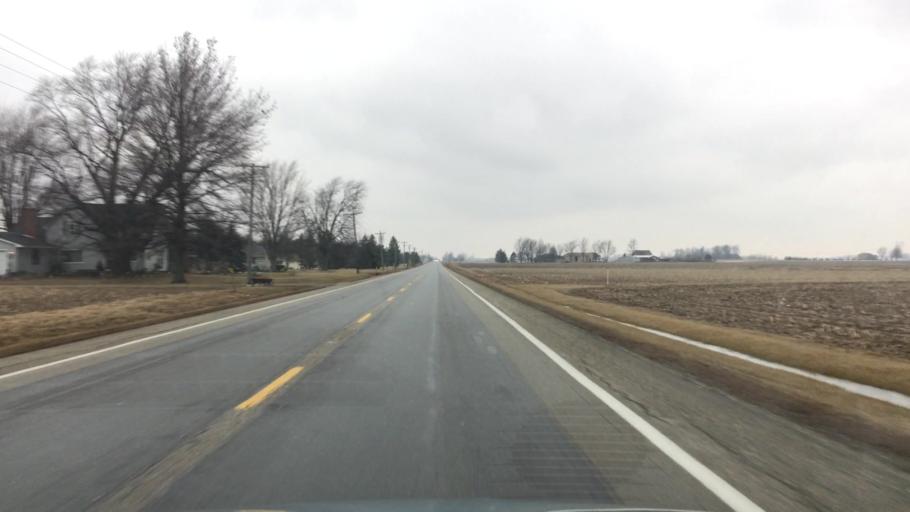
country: US
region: Ohio
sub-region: Auglaize County
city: Saint Marys
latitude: 40.5783
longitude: -84.4503
